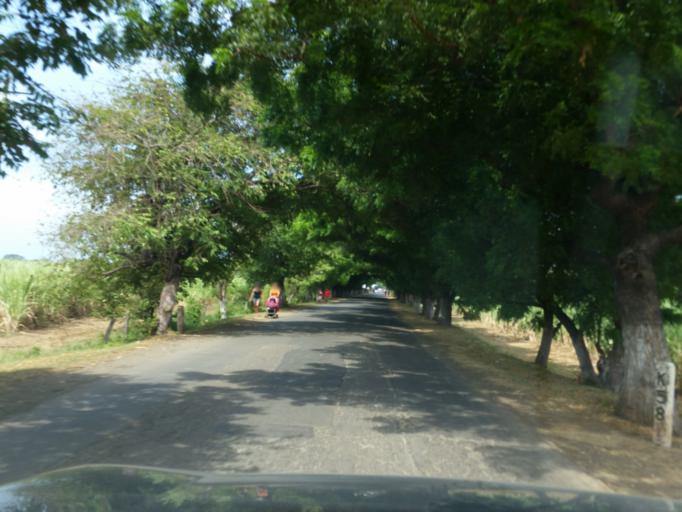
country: NI
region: Managua
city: Masachapa
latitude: 11.7880
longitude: -86.5090
